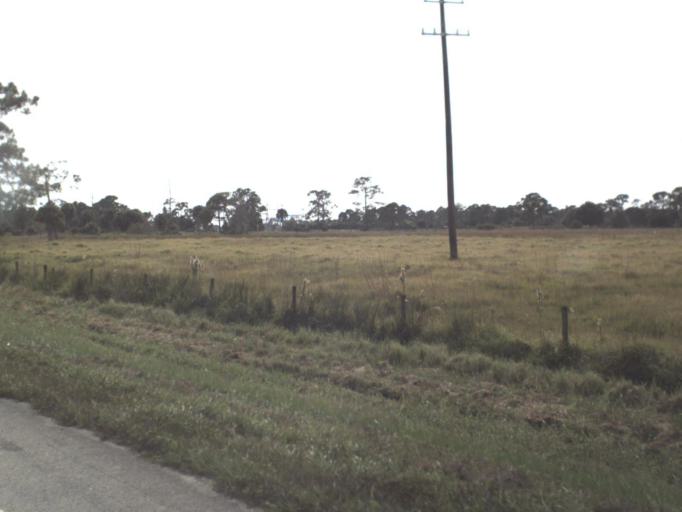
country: US
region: Florida
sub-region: Okeechobee County
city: Cypress Quarters
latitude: 27.2919
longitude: -80.8279
